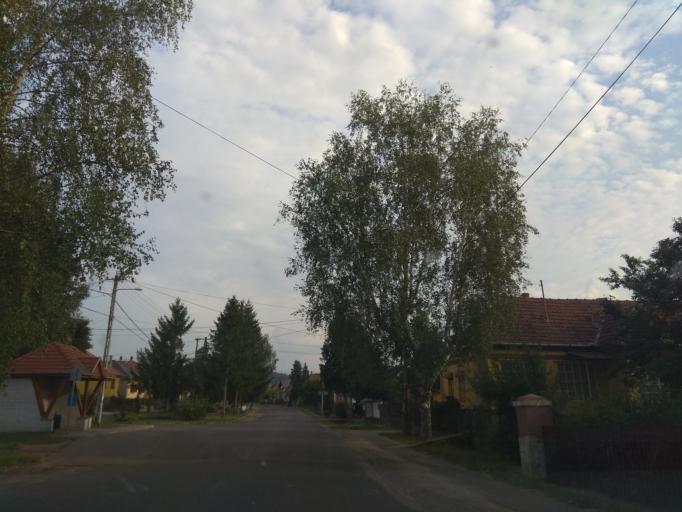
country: HU
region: Heves
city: Petervasara
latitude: 48.0403
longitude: 20.1027
